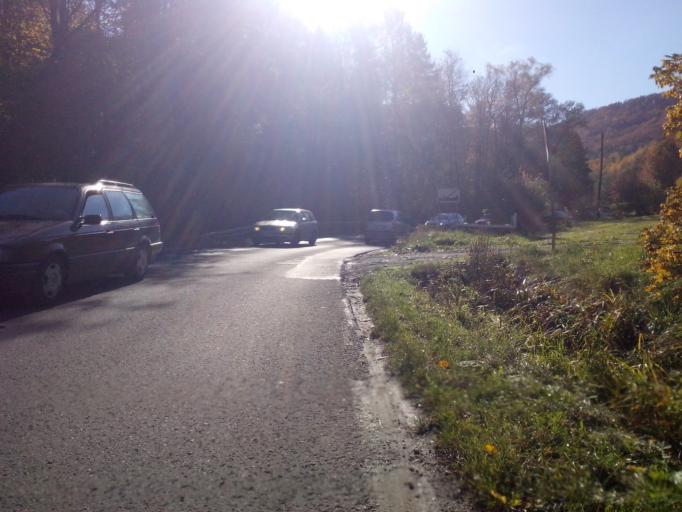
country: PL
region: Subcarpathian Voivodeship
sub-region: Powiat krosnienski
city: Korczyna
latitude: 49.7642
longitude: 21.7985
